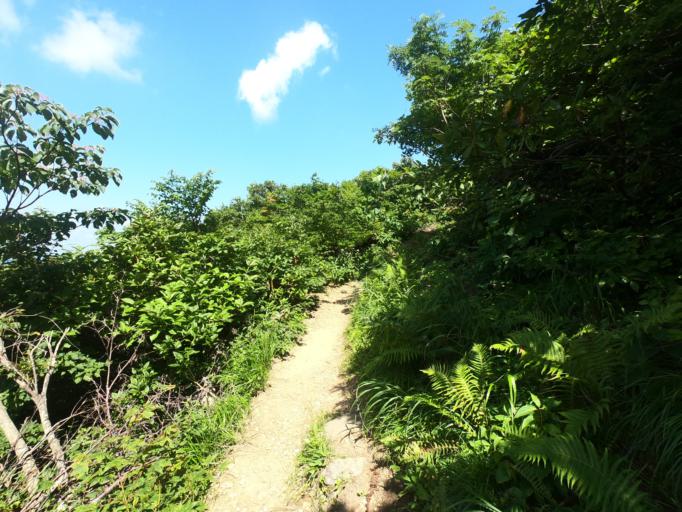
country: JP
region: Akita
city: Yuzawa
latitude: 38.9781
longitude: 140.7748
